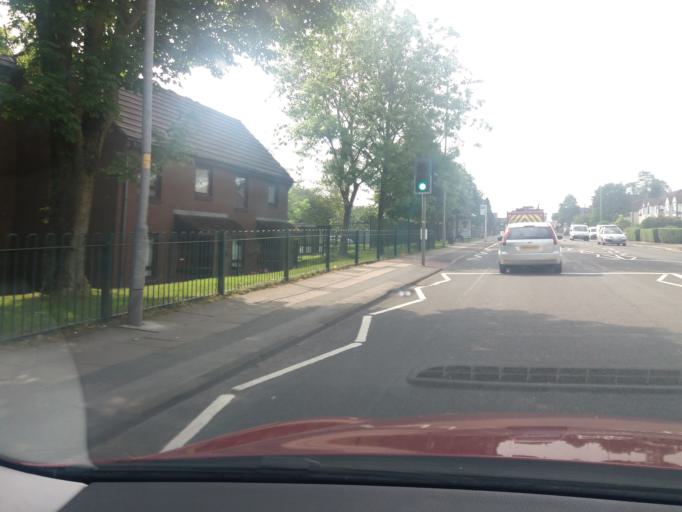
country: GB
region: England
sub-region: Borough of Bolton
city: Horwich
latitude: 53.5873
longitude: -2.5292
